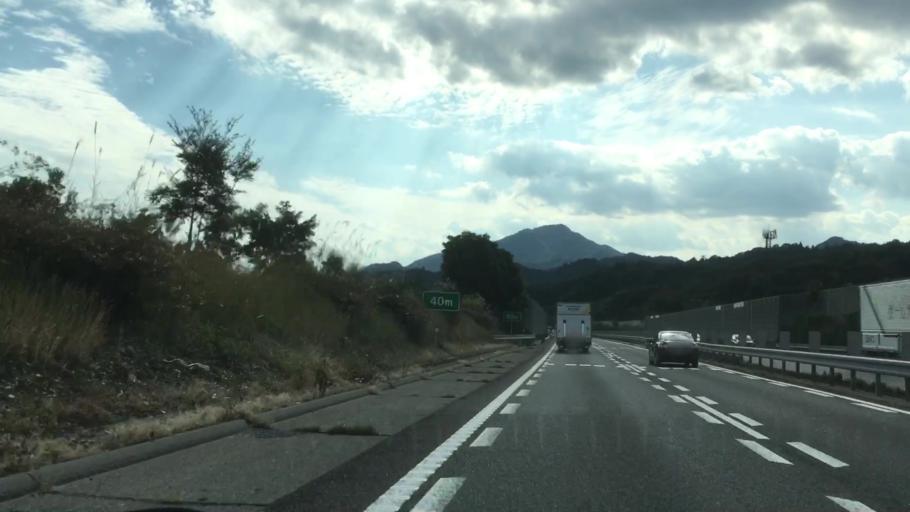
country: JP
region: Hiroshima
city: Miyajima
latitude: 34.3224
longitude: 132.2874
